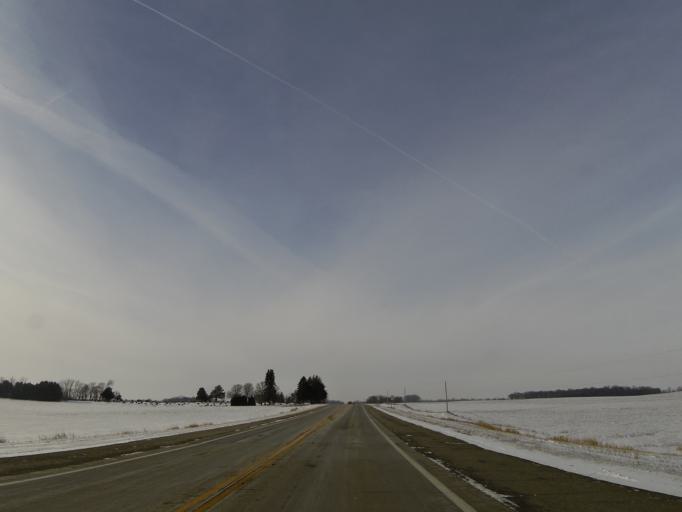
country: US
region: Minnesota
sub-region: McLeod County
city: Hutchinson
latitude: 44.8924
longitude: -94.2386
